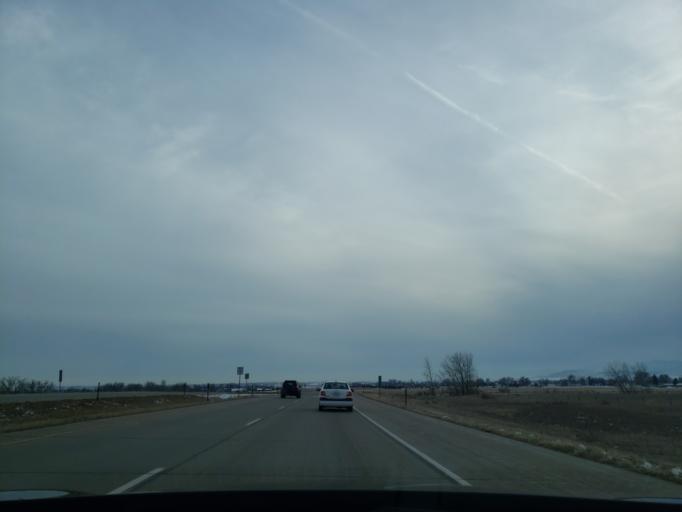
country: US
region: Colorado
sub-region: Larimer County
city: Berthoud
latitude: 40.3229
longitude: -105.1026
